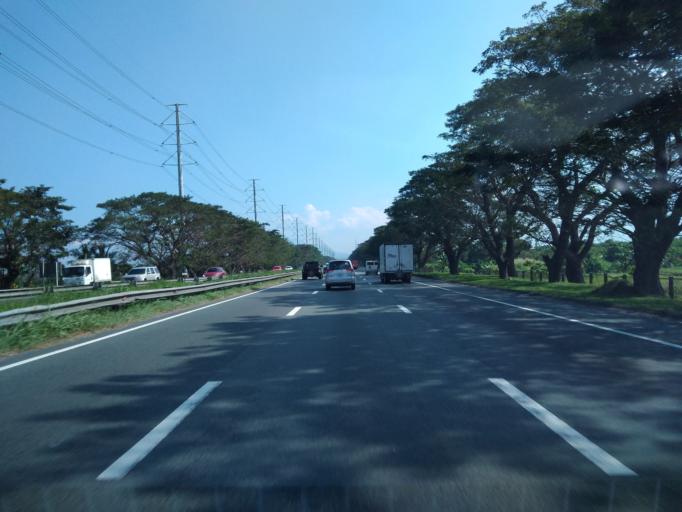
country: PH
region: Calabarzon
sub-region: Province of Laguna
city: Pulong Santa Cruz
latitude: 14.2654
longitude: 121.0984
